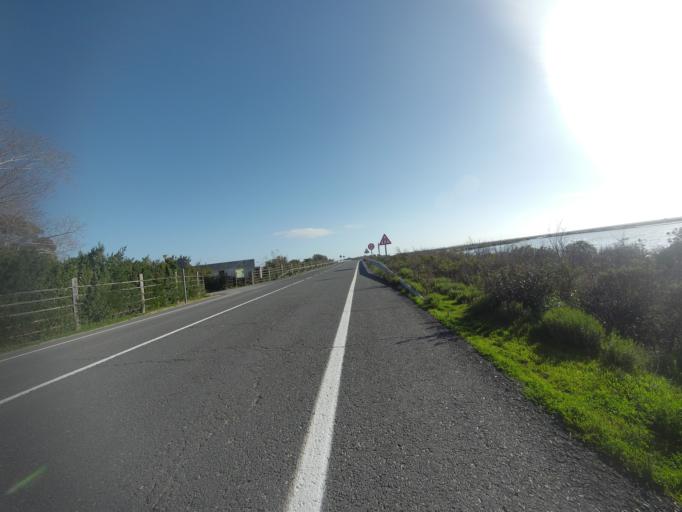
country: ES
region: Andalusia
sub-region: Provincia de Huelva
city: Huelva
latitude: 37.2524
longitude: -6.9690
